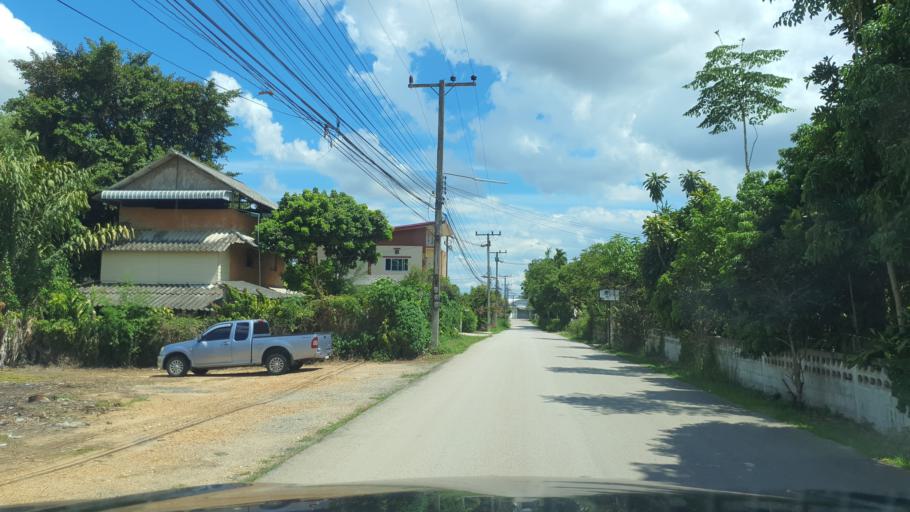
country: TH
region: Chiang Mai
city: San Sai
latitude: 18.8958
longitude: 99.0387
